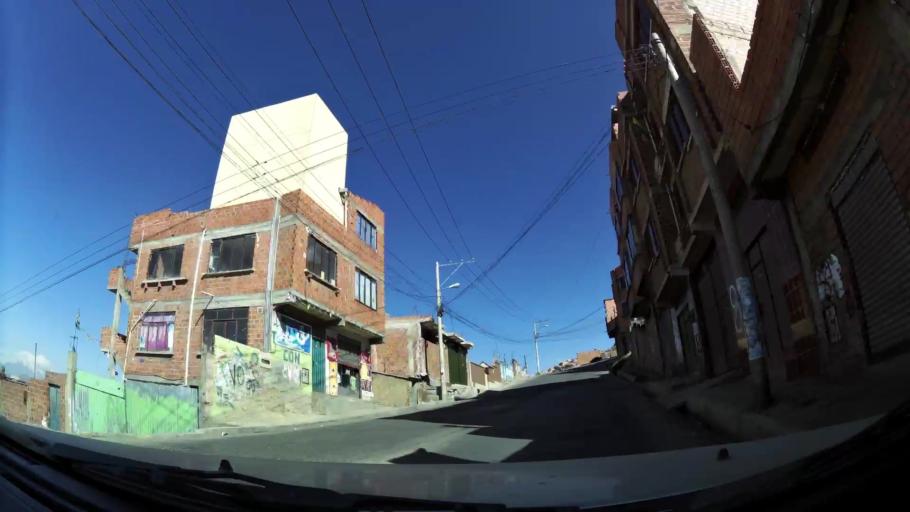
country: BO
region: La Paz
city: La Paz
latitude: -16.5212
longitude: -68.1424
